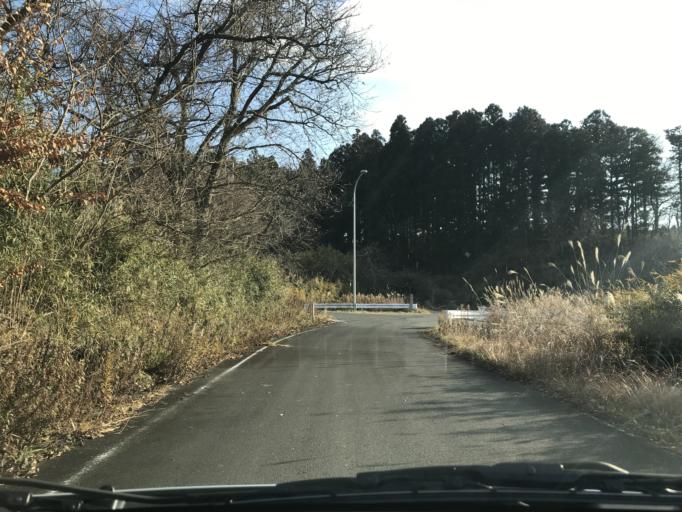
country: JP
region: Miyagi
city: Wakuya
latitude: 38.6864
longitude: 141.1101
